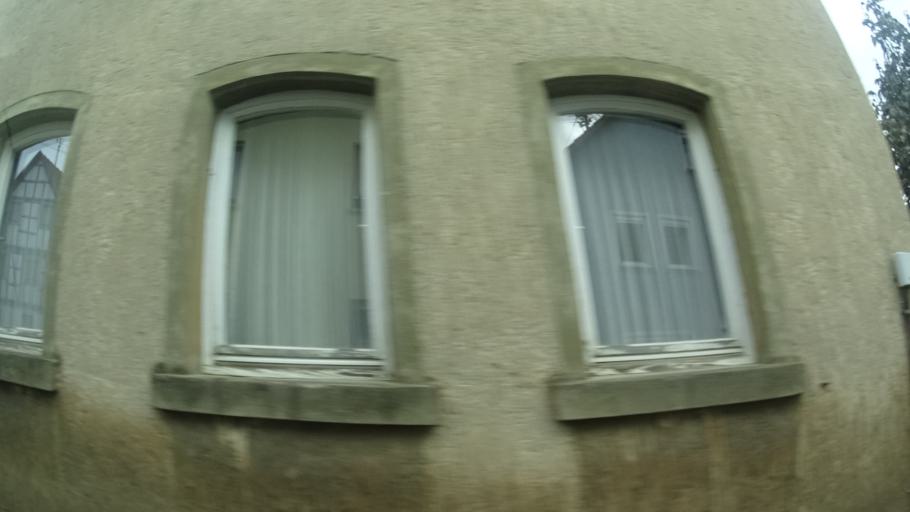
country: DE
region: Bavaria
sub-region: Regierungsbezirk Unterfranken
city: Hochheim
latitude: 50.3636
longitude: 10.4477
